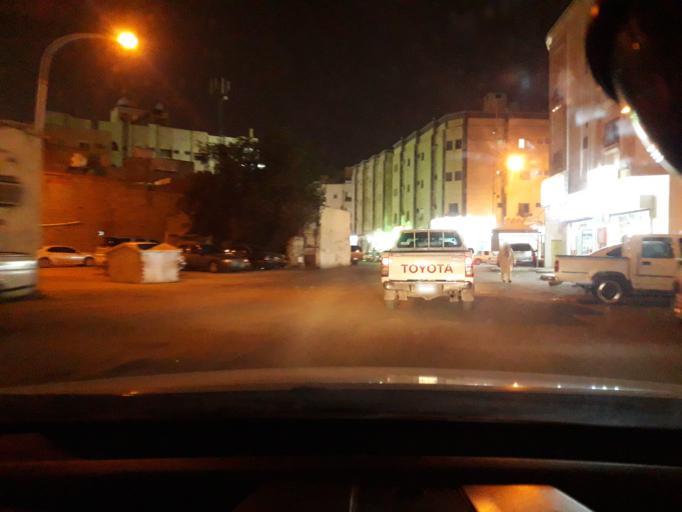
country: SA
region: Al Madinah al Munawwarah
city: Medina
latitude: 24.4666
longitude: 39.6279
